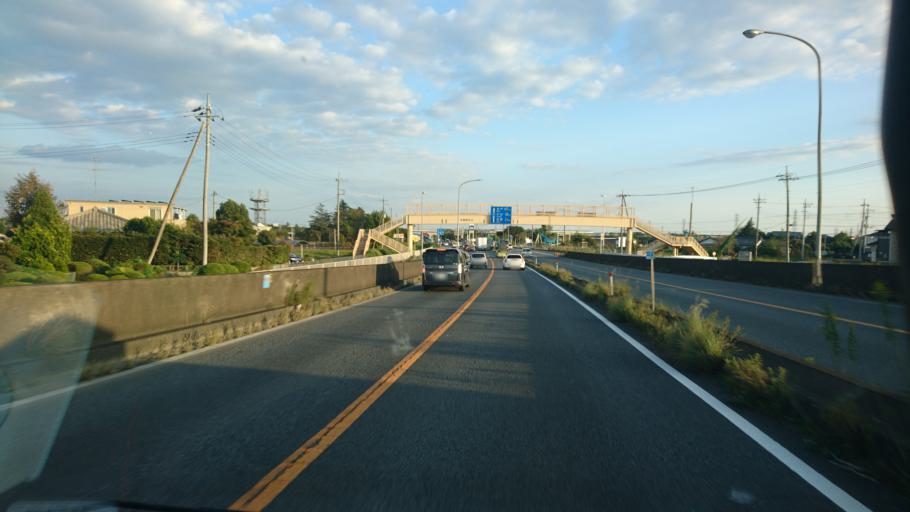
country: JP
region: Gunma
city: Ota
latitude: 36.3364
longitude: 139.3894
